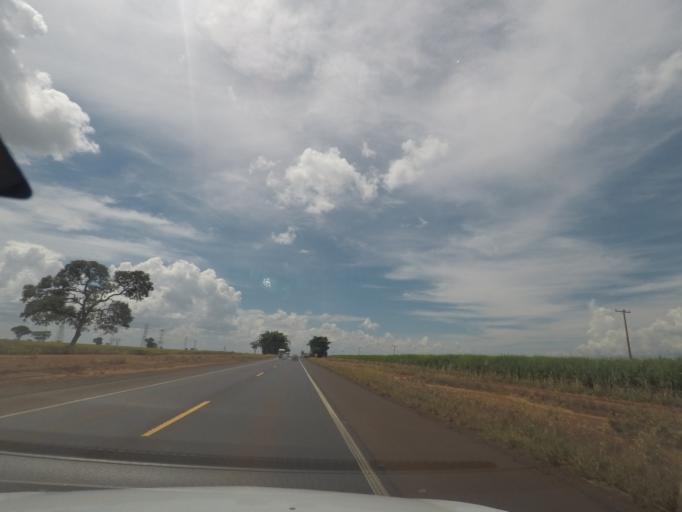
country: BR
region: Sao Paulo
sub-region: Barretos
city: Barretos
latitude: -20.2783
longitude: -48.6717
